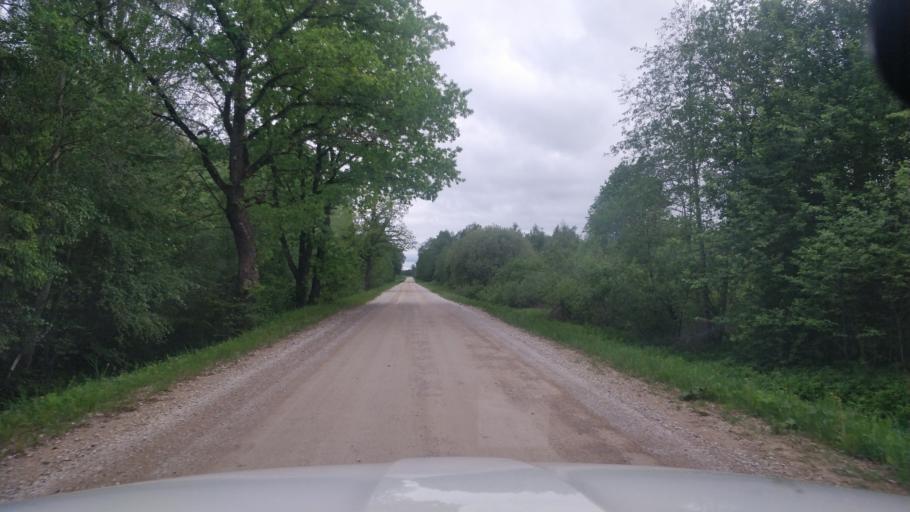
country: EE
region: Raplamaa
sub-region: Maerjamaa vald
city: Marjamaa
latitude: 58.7628
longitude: 24.2506
